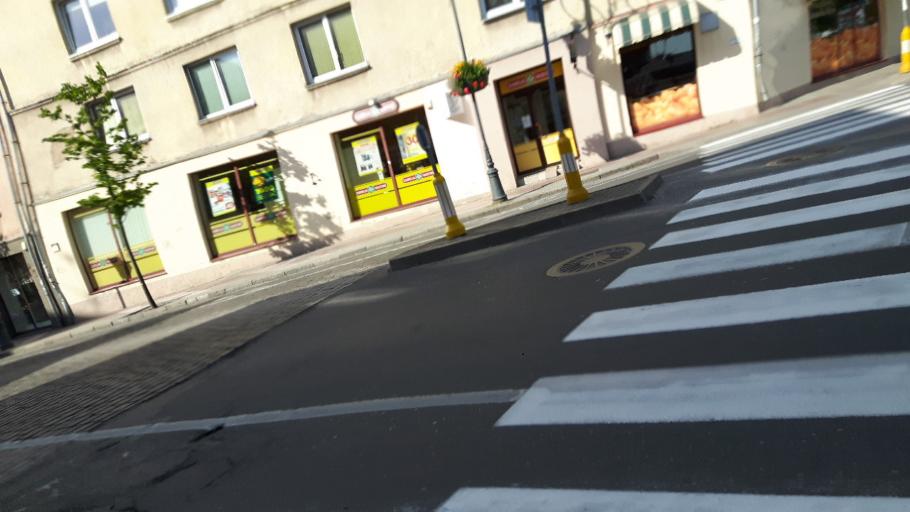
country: LT
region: Klaipedos apskritis
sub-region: Klaipeda
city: Klaipeda
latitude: 55.7071
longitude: 21.1384
